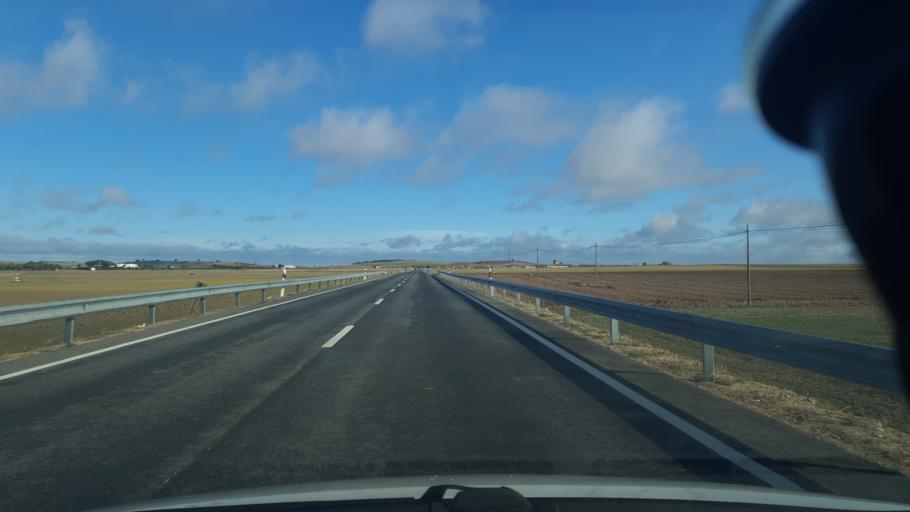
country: ES
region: Castille and Leon
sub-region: Provincia de Segovia
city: Codorniz
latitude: 41.0574
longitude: -4.6168
